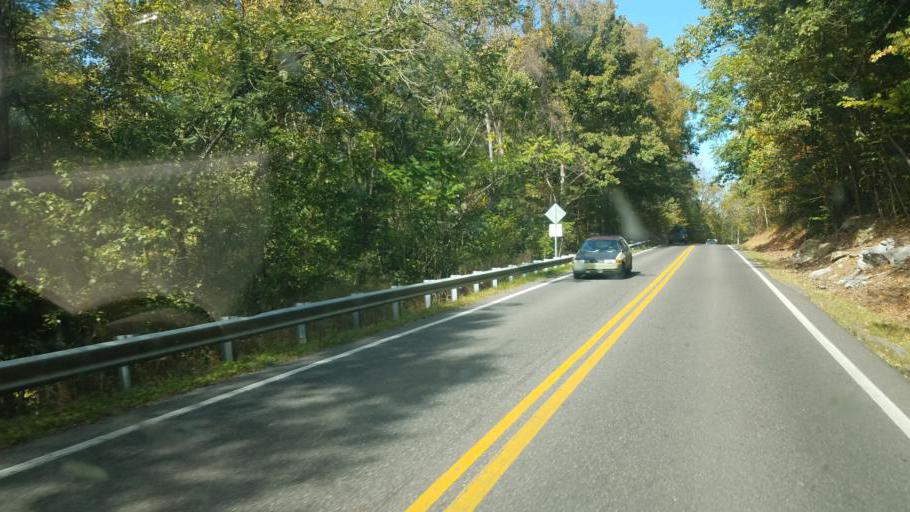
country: US
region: Virginia
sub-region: Page County
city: Luray
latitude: 38.7977
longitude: -78.3600
